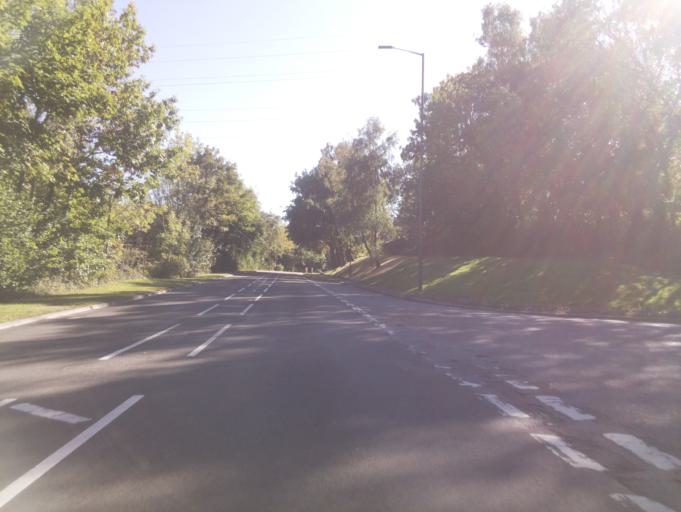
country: GB
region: Wales
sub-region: Torfaen County Borough
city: Cwmbran
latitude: 51.6570
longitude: -3.0454
